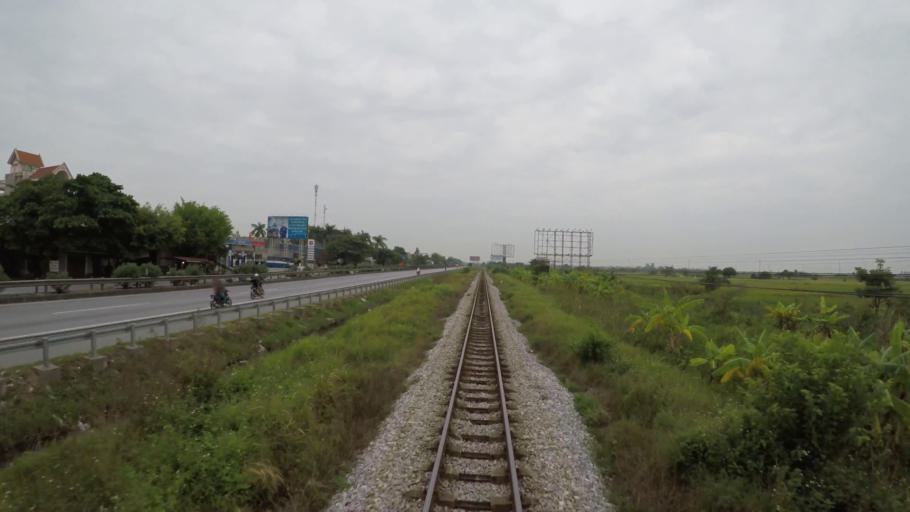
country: VN
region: Hai Duong
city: Phu Thai
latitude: 20.9384
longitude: 106.5477
